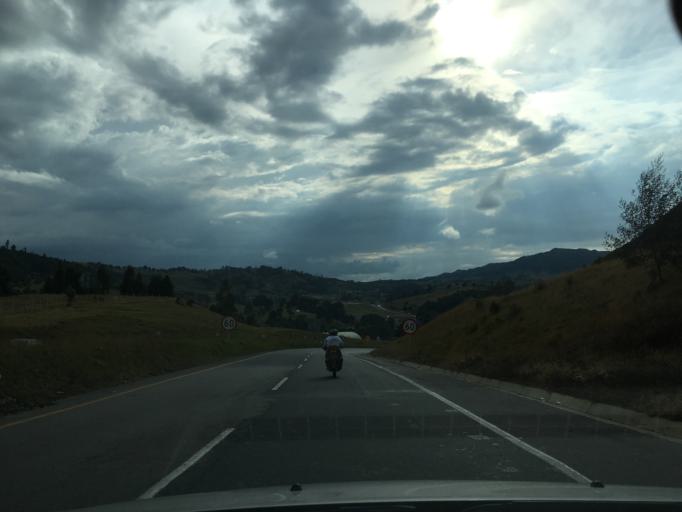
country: CO
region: Boyaca
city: Samaca
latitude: 5.4549
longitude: -73.4228
